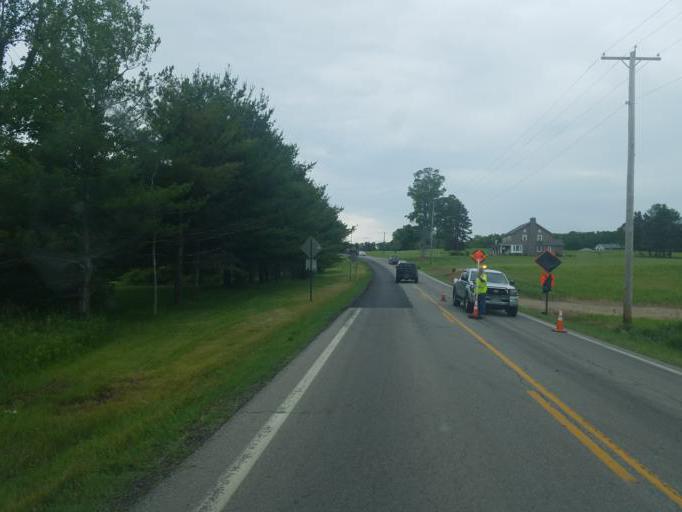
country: US
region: Ohio
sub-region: Richland County
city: Lexington
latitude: 40.6151
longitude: -82.5900
